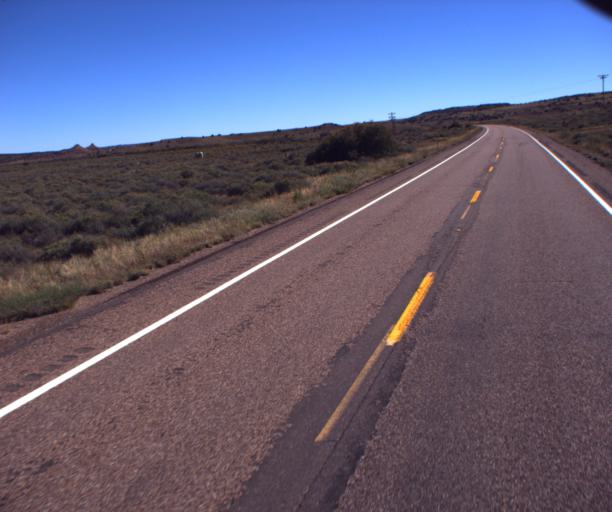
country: US
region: Arizona
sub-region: Apache County
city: Saint Johns
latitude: 34.5855
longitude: -109.5780
